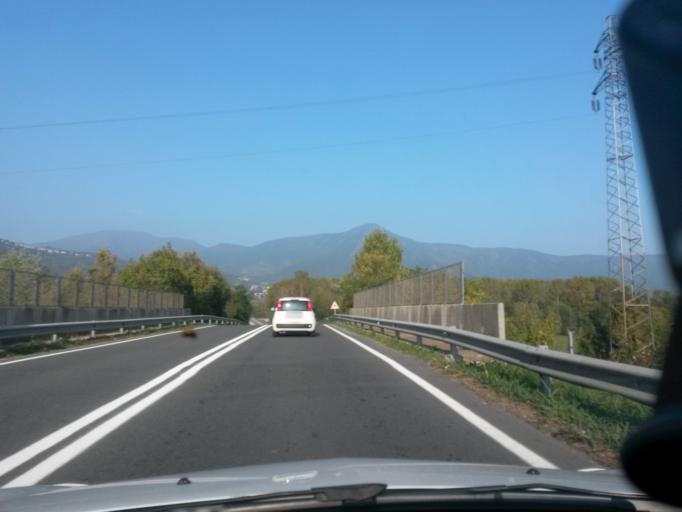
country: IT
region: Piedmont
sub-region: Provincia di Torino
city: Sant'Ambrogio di Torino
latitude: 45.0967
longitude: 7.3711
